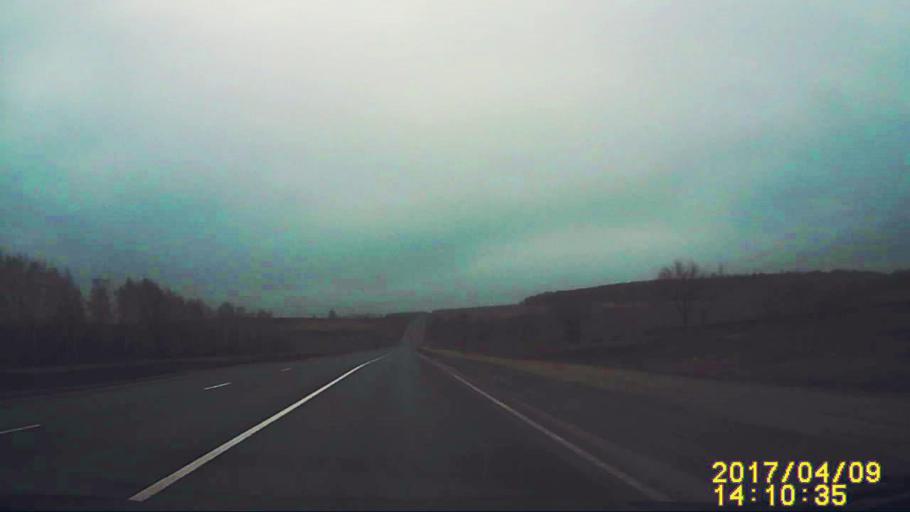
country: RU
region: Ulyanovsk
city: Krasnyy Gulyay
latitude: 54.0398
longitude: 48.2137
